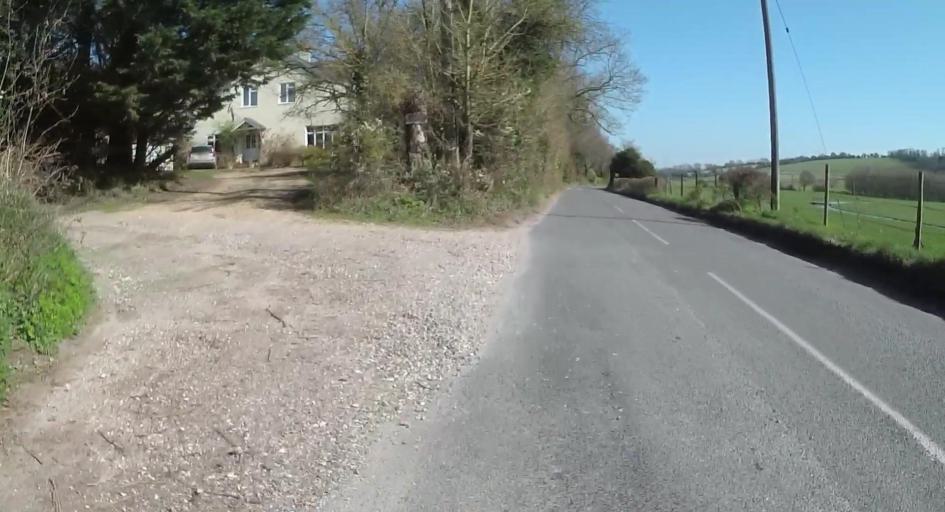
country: GB
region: England
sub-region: Hampshire
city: Andover
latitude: 51.2734
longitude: -1.4438
